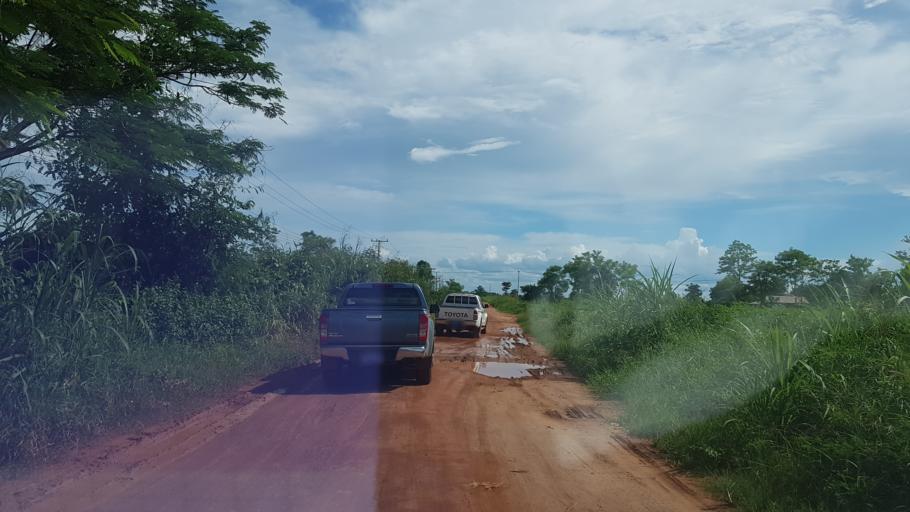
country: LA
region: Vientiane
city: Vientiane
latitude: 18.2159
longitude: 102.5678
